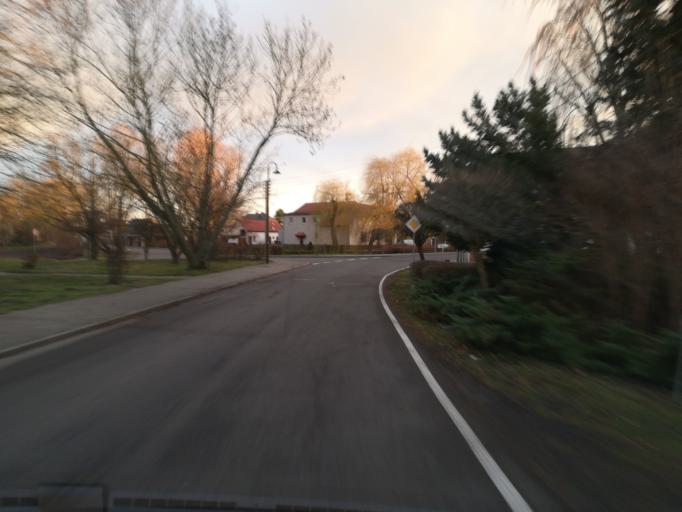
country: DE
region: Saxony
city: Wiedemar
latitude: 51.4992
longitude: 12.2282
